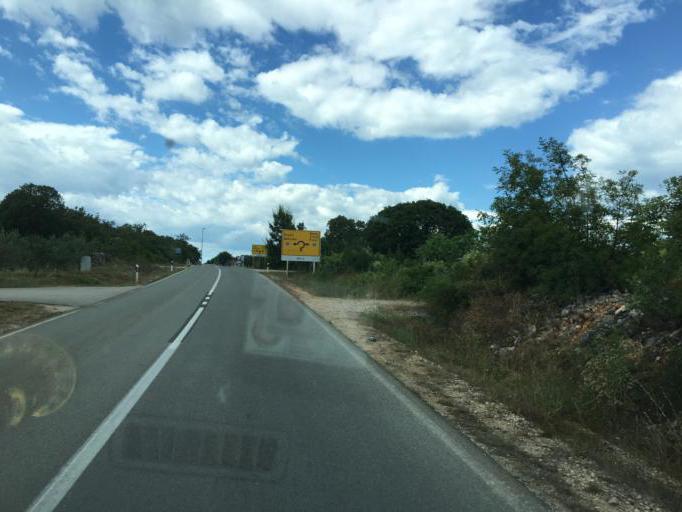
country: HR
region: Primorsko-Goranska
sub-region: Grad Krk
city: Krk
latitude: 45.0401
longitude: 14.5697
